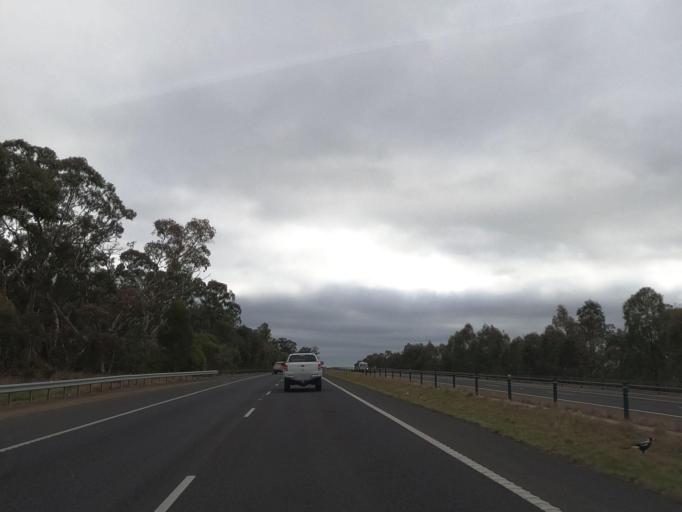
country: AU
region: Victoria
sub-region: Mount Alexander
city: Castlemaine
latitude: -37.0316
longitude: 144.2749
